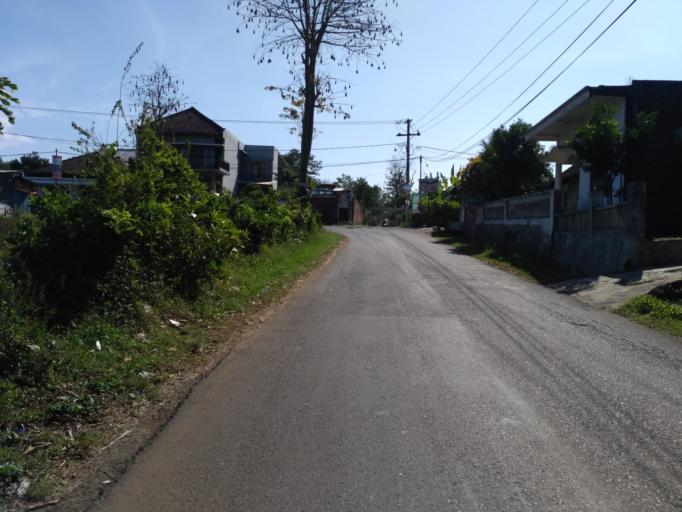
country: ID
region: East Java
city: Singosari
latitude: -7.9217
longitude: 112.6676
